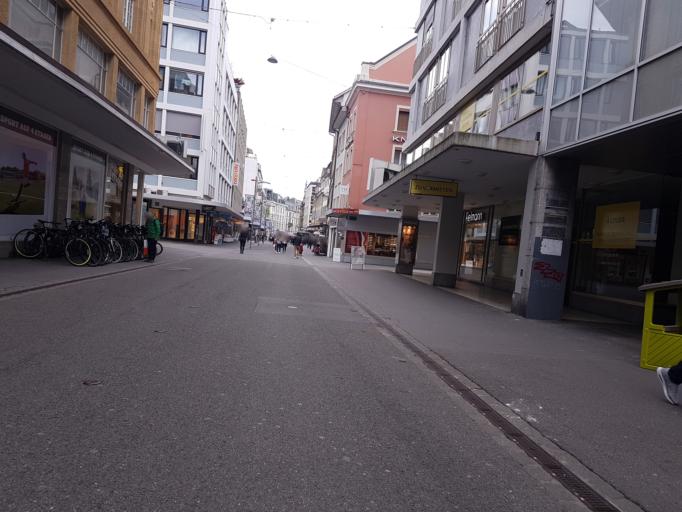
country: CH
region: Bern
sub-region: Biel/Bienne District
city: Biel/Bienne
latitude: 47.1402
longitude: 7.2454
